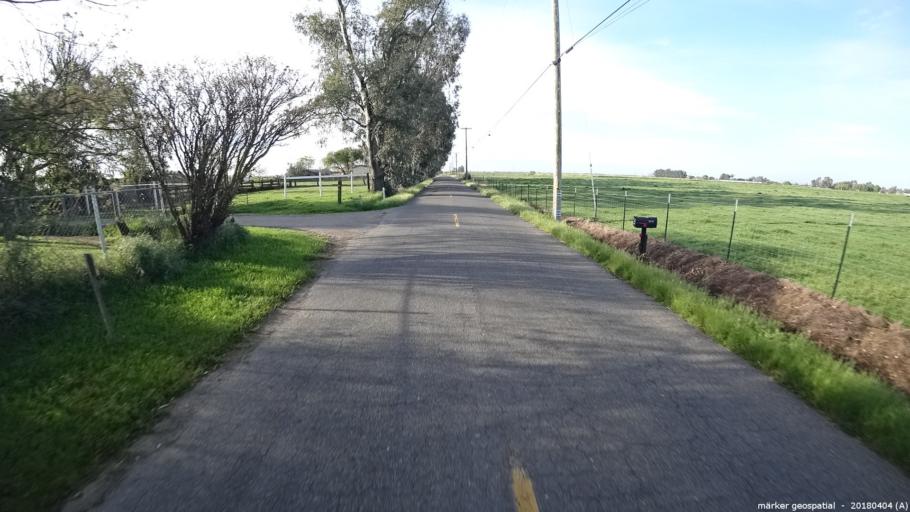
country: US
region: California
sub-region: Sacramento County
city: Herald
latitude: 38.3397
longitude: -121.2539
